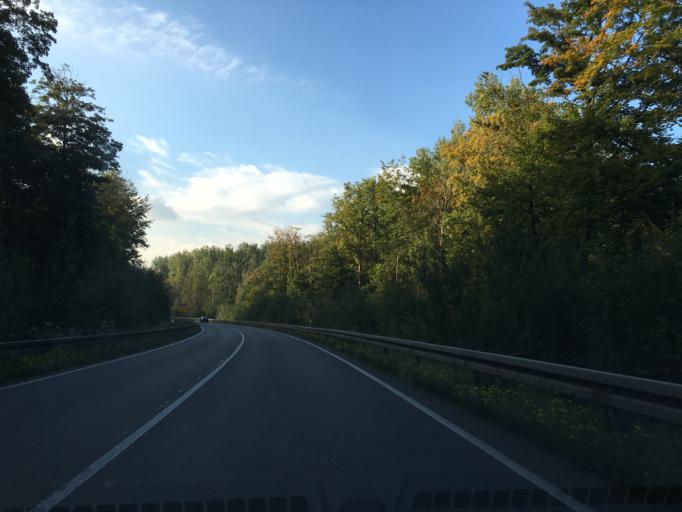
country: DE
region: North Rhine-Westphalia
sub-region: Regierungsbezirk Munster
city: Dulmen
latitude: 51.8445
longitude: 7.3115
